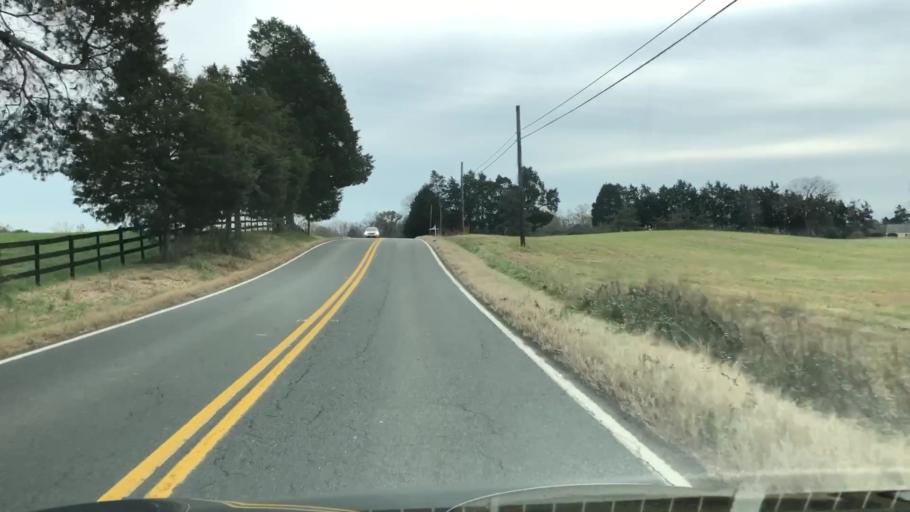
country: US
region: Virginia
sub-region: Fauquier County
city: New Baltimore
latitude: 38.7590
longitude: -77.6778
